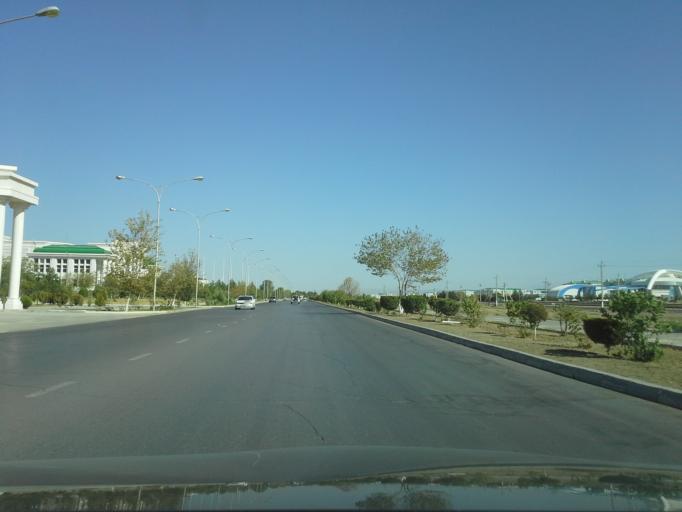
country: TM
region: Ahal
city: Ashgabat
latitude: 37.9911
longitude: 58.3219
